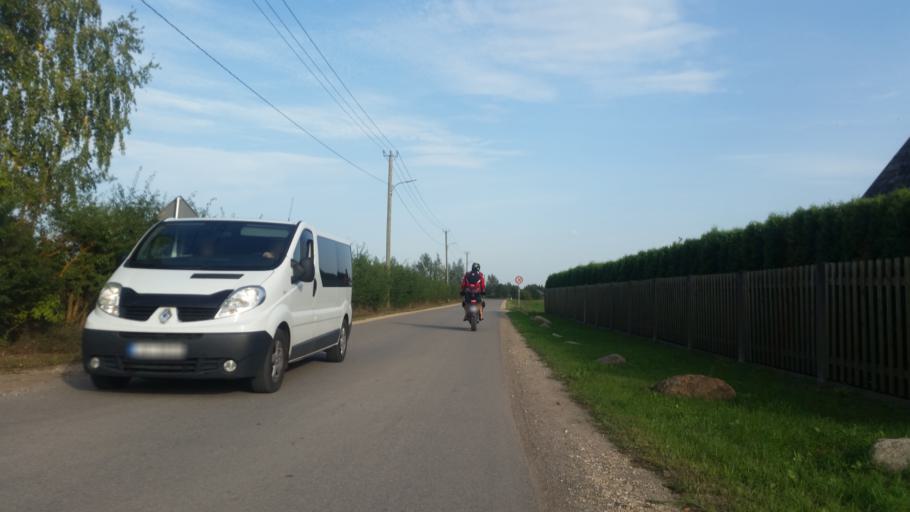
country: LV
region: Ikskile
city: Ikskile
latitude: 56.8191
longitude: 24.5123
